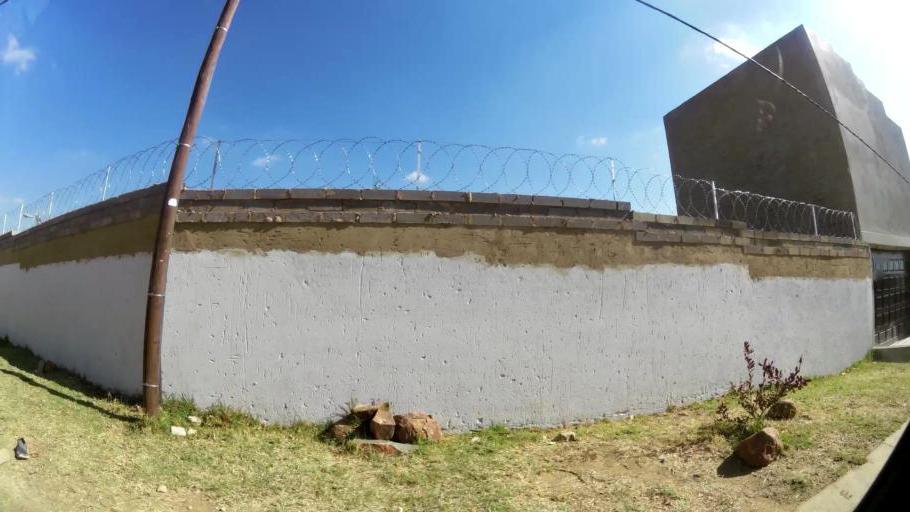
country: ZA
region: Gauteng
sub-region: West Rand District Municipality
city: Muldersdriseloop
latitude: -26.0243
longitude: 27.9345
